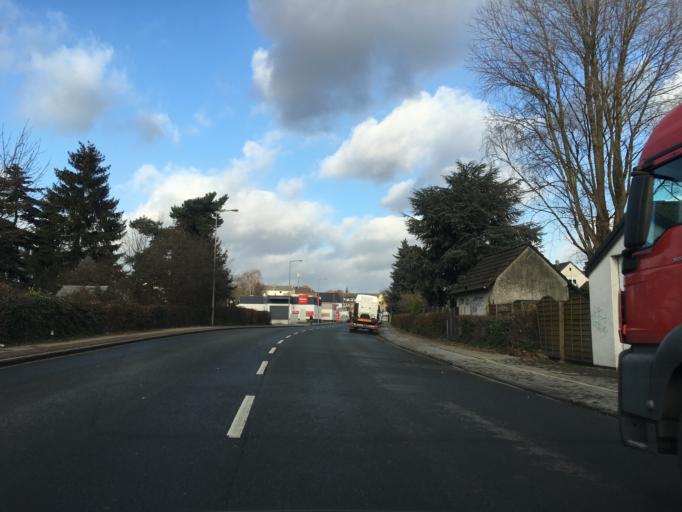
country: DE
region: North Rhine-Westphalia
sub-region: Regierungsbezirk Dusseldorf
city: Oberhausen
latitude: 51.5081
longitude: 6.8360
